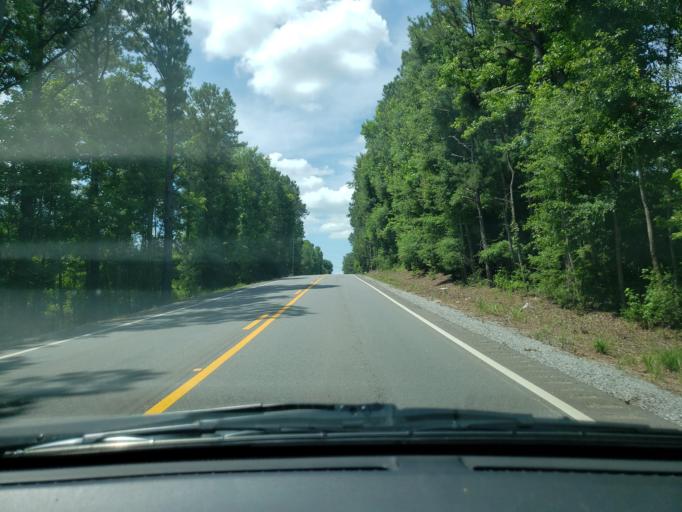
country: US
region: Alabama
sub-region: Elmore County
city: Eclectic
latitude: 32.6262
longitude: -85.9498
